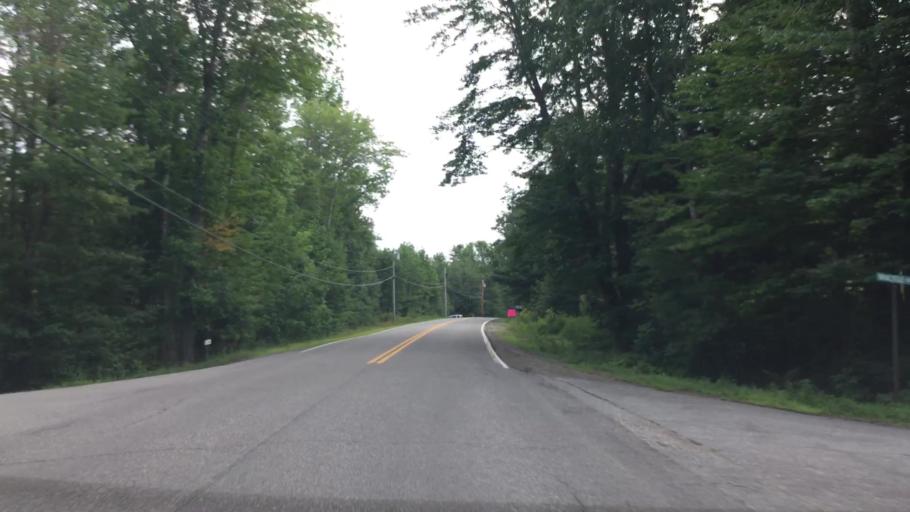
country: US
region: Maine
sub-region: Waldo County
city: Lincolnville
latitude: 44.3385
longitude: -69.0558
